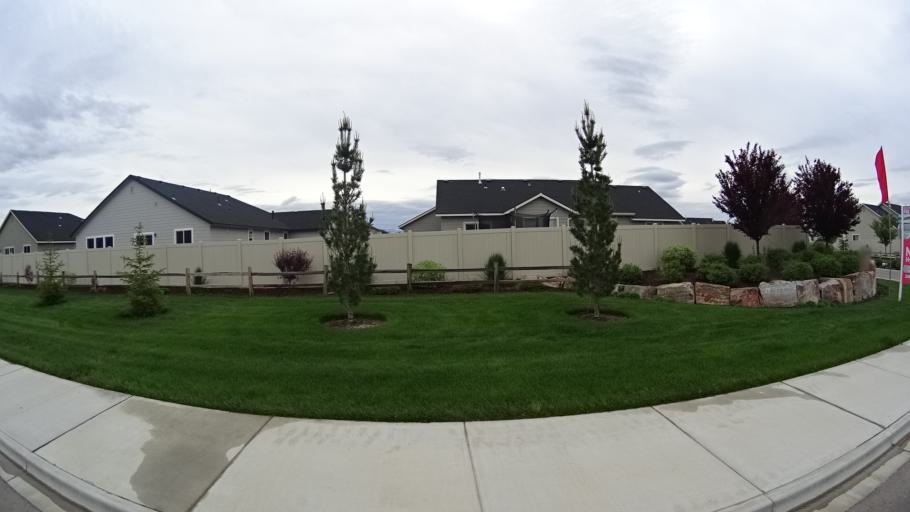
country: US
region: Idaho
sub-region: Ada County
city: Star
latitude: 43.7129
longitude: -116.5032
